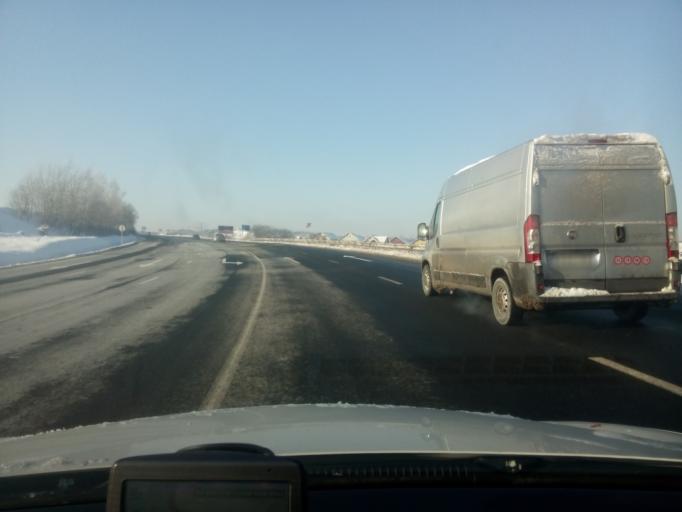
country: RO
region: Sibiu
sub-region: Comuna Selimbar
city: Selimbar
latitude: 45.7587
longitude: 24.1978
